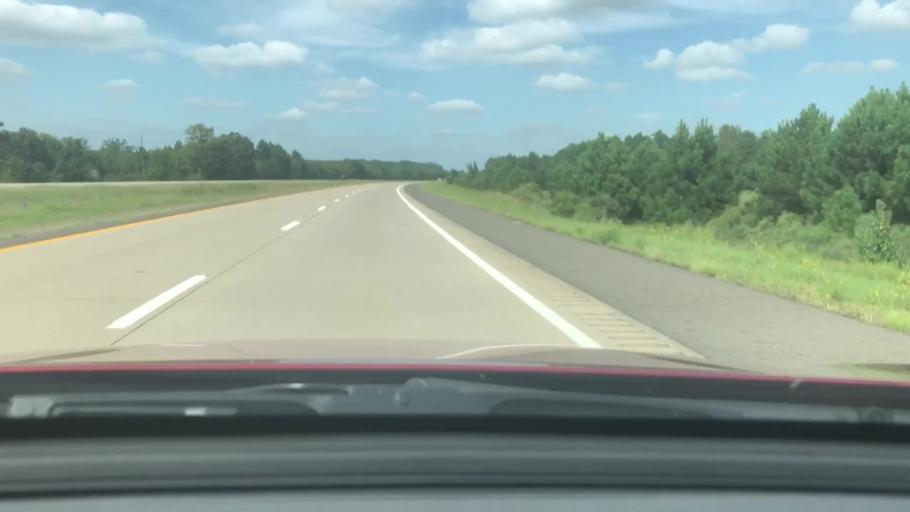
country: US
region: Texas
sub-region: Cass County
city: Queen City
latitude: 33.1998
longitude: -93.8783
